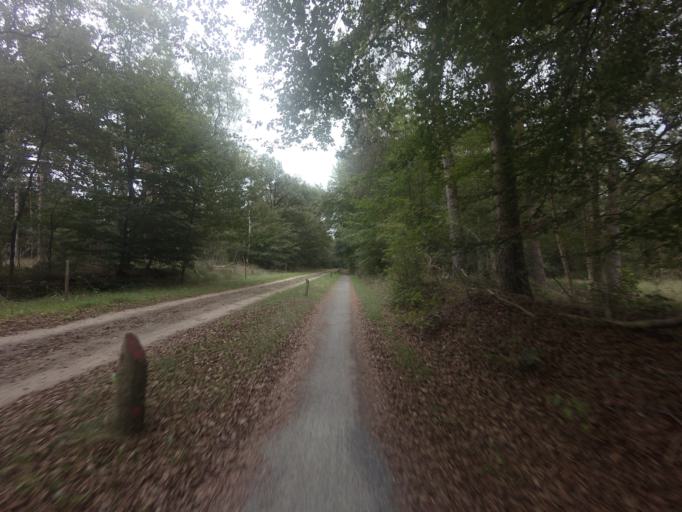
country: NL
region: Drenthe
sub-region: Gemeente Westerveld
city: Dwingeloo
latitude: 52.8792
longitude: 6.2702
